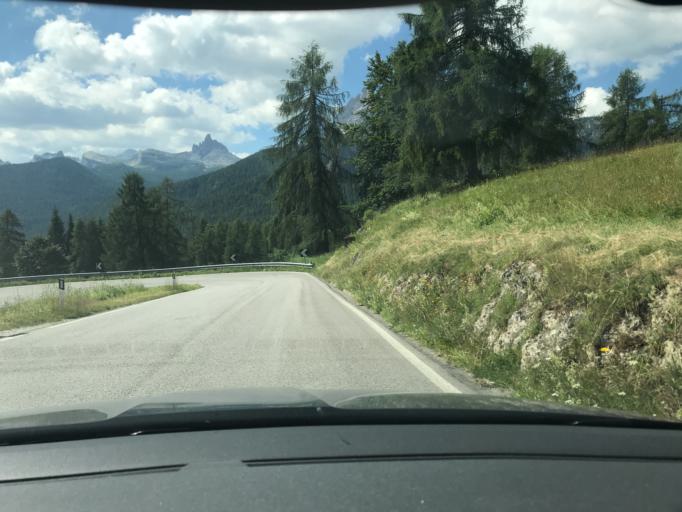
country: IT
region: Veneto
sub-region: Provincia di Belluno
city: Cortina d'Ampezzo
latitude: 46.5235
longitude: 12.1137
